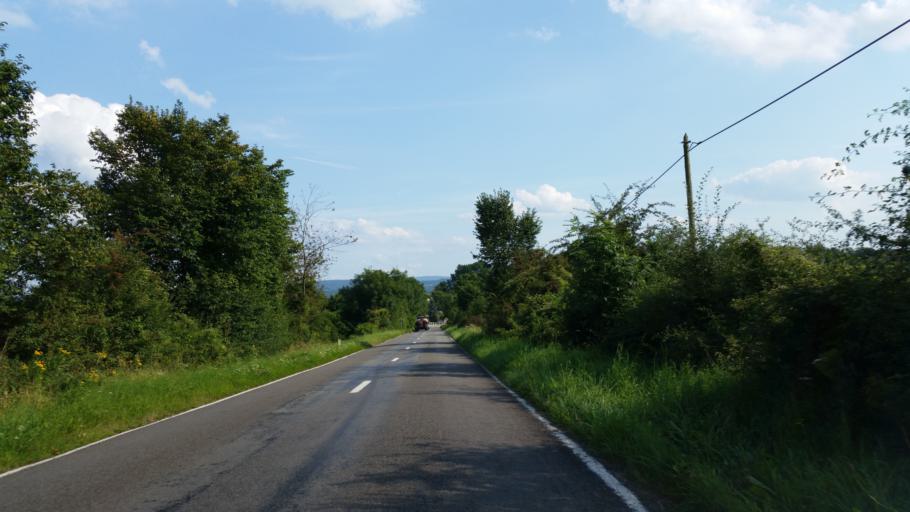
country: BE
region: Wallonia
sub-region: Province du Luxembourg
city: Durbuy
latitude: 50.3789
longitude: 5.4654
